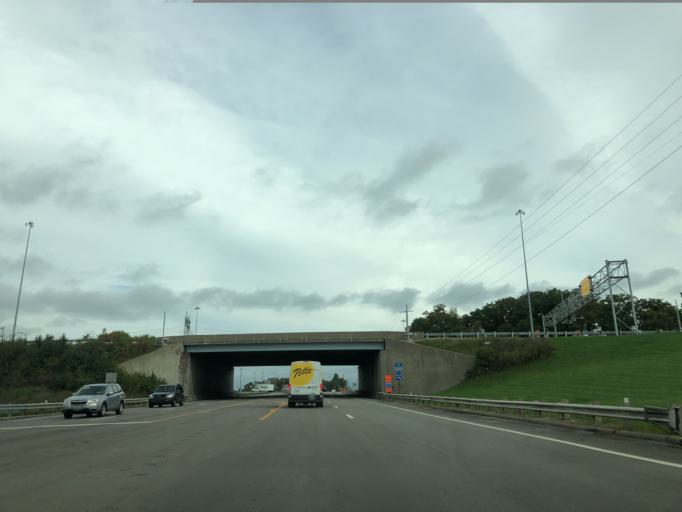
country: US
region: Ohio
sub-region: Summit County
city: Richfield
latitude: 41.2701
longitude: -81.6286
